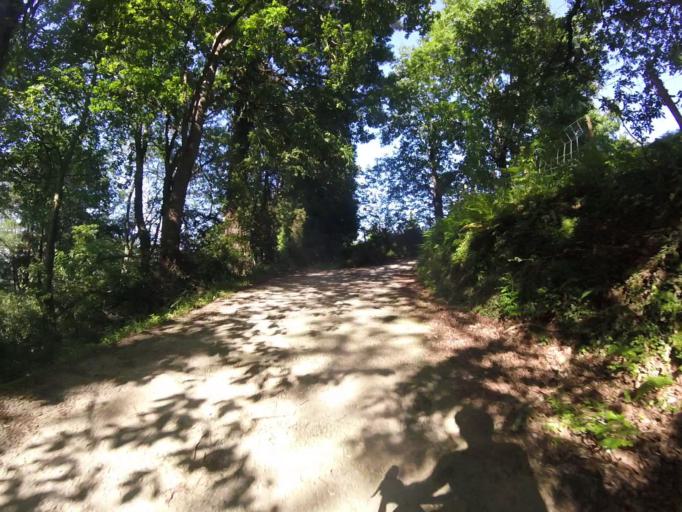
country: ES
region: Basque Country
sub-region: Provincia de Guipuzcoa
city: Irun
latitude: 43.3106
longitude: -1.7804
